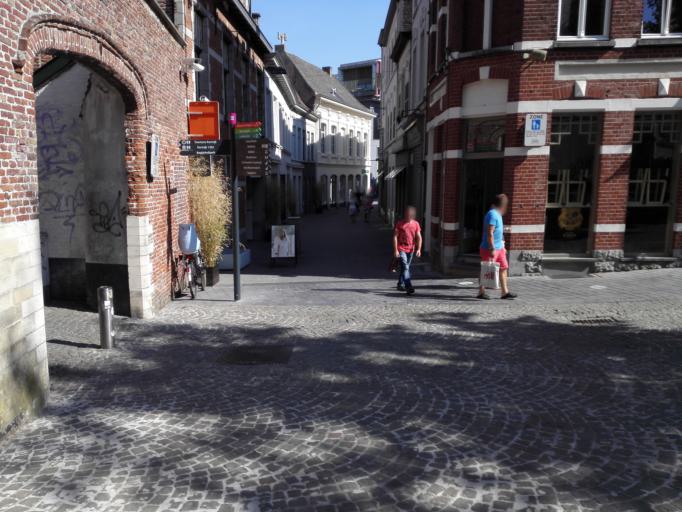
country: BE
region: Flanders
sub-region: Provincie West-Vlaanderen
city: Kortrijk
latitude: 50.8274
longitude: 3.2686
